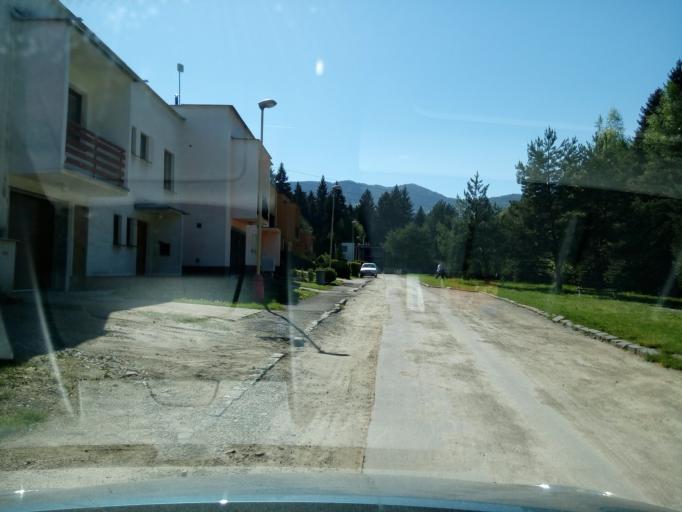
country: SK
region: Zilinsky
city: Ruzomberok
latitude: 49.0800
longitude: 19.2839
